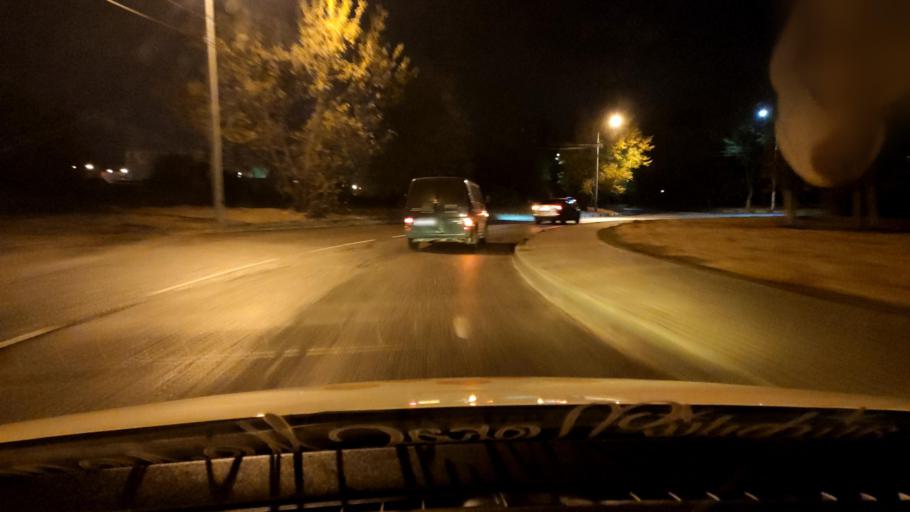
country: RU
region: Voronezj
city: Voronezh
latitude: 51.6590
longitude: 39.1314
